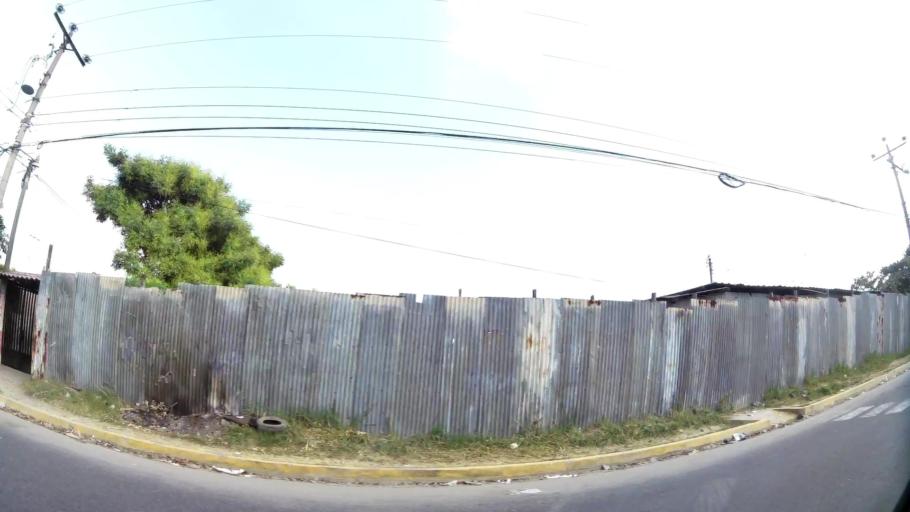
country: SV
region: San Salvador
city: Soyapango
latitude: 13.7181
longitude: -89.1430
